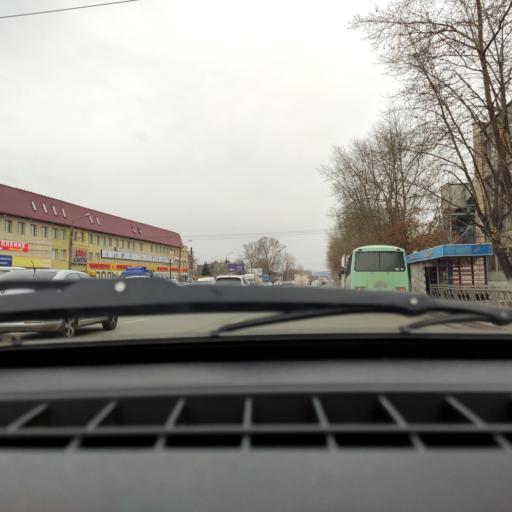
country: RU
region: Bashkortostan
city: Ufa
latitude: 54.8064
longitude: 56.0836
